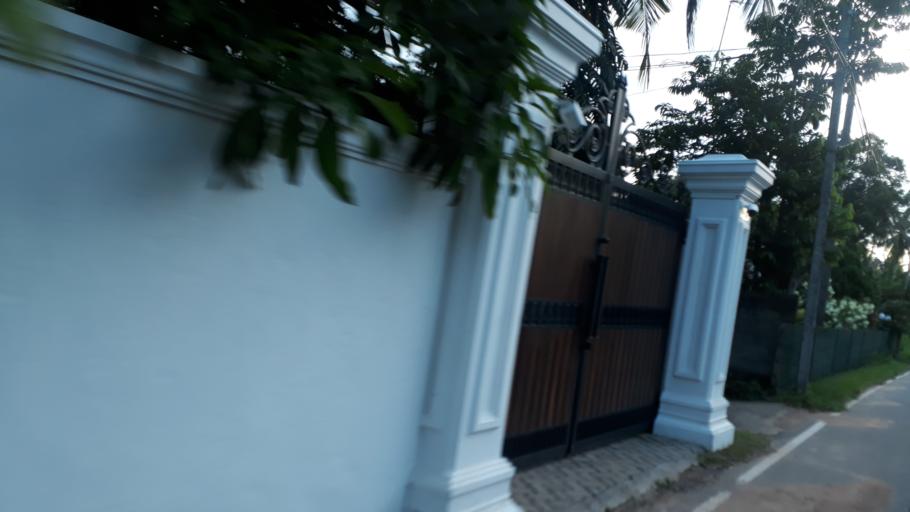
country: LK
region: Western
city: Gampaha
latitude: 7.1024
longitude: 79.9878
